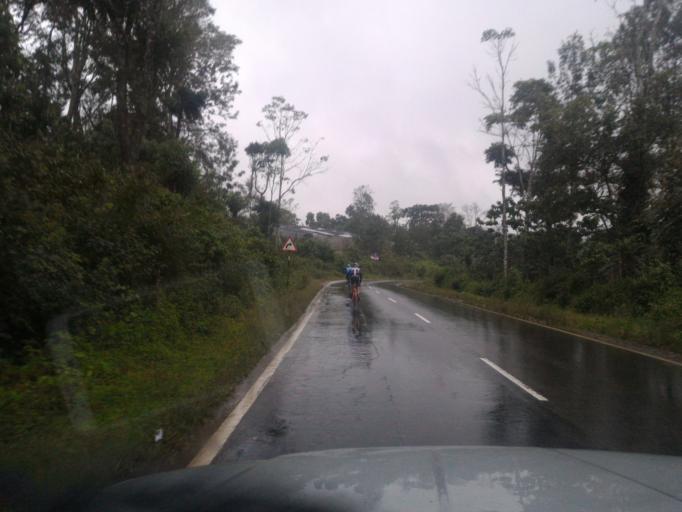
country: IN
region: Karnataka
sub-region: Kodagu
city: Suntikoppa
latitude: 12.4397
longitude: 75.7909
